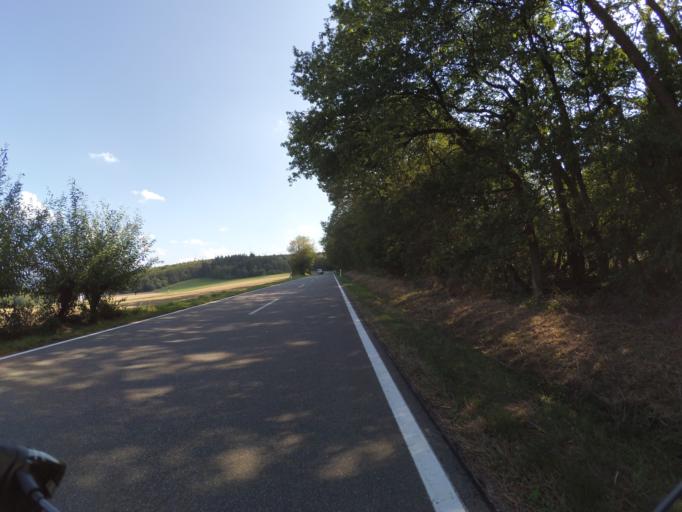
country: DE
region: Rheinland-Pfalz
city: Wintrich
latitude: 49.8682
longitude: 6.9629
